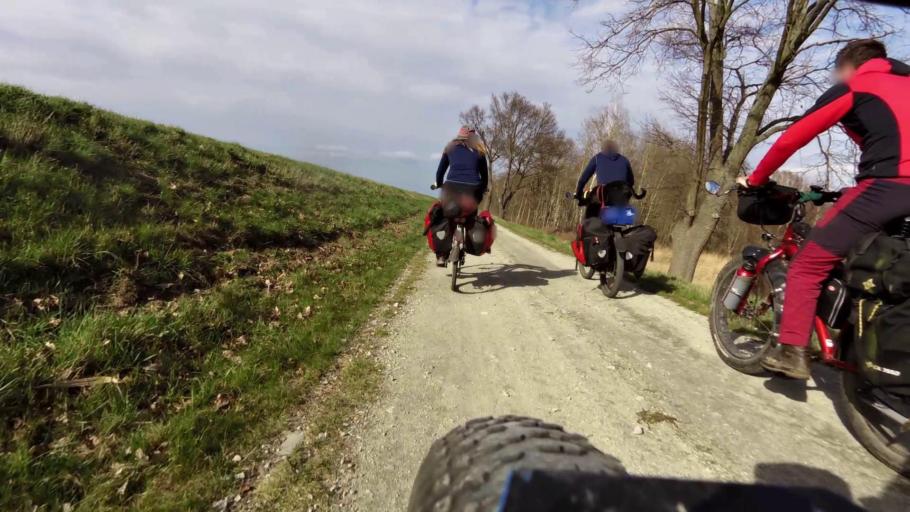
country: DE
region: Brandenburg
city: Reitwein
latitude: 52.5275
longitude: 14.6105
